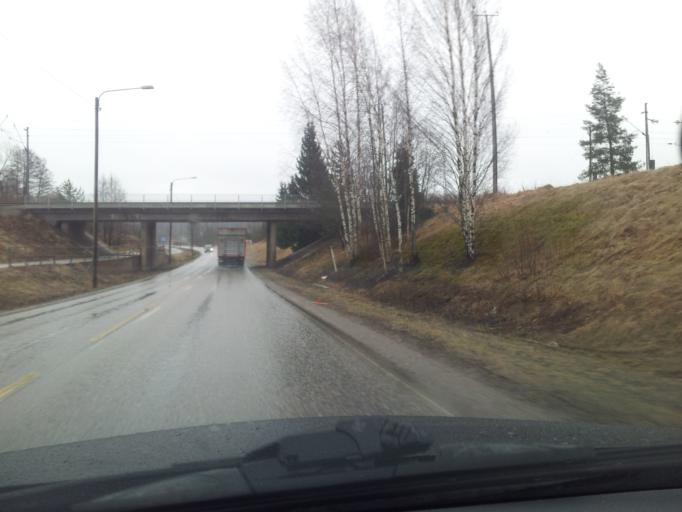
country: FI
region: Uusimaa
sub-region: Helsinki
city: Kirkkonummi
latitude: 60.1543
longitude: 24.5336
